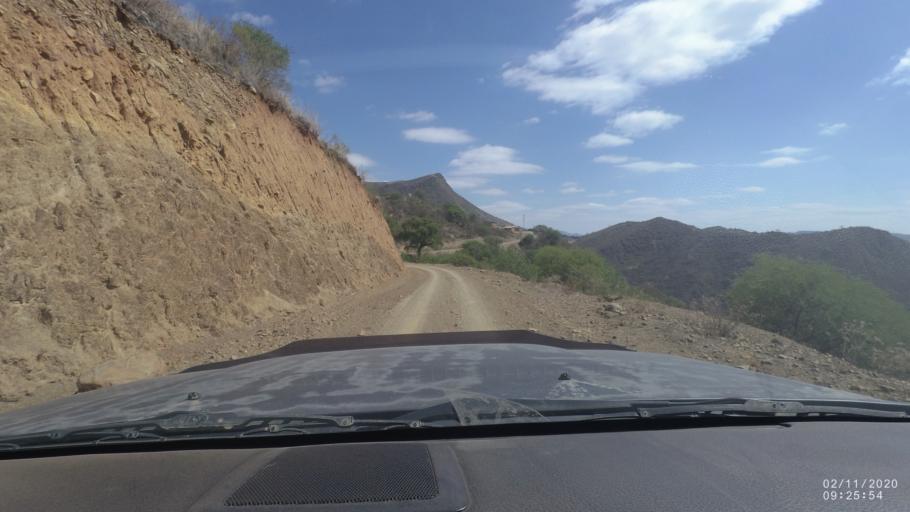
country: BO
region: Chuquisaca
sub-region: Provincia Zudanez
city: Mojocoya
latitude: -18.4526
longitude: -64.5835
